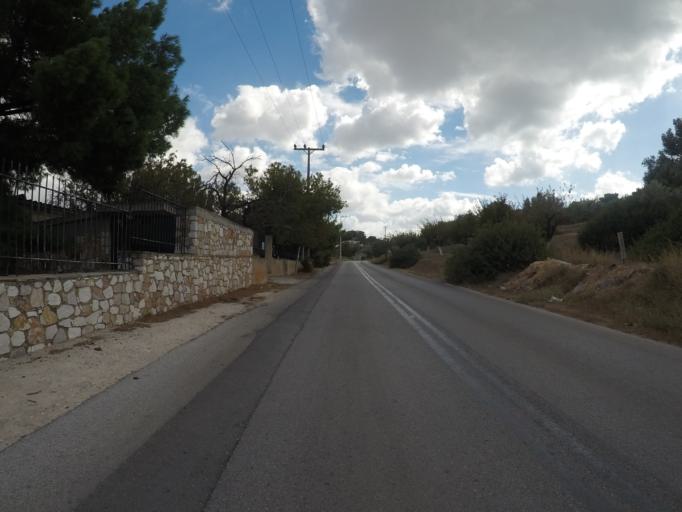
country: GR
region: Attica
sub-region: Nomarchia Anatolikis Attikis
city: Agios Dimitrios Kropias
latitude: 37.8206
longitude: 23.8635
